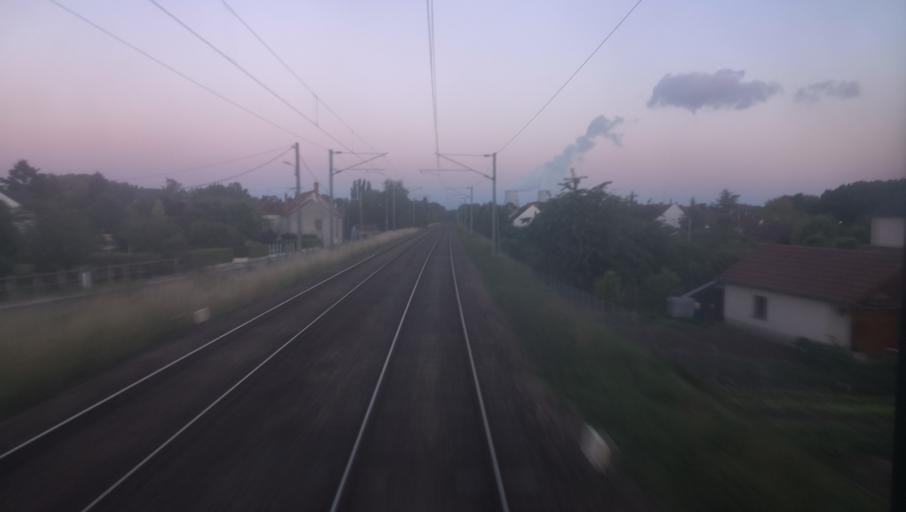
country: FR
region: Centre
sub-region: Departement du Loiret
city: Bonny-sur-Loire
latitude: 47.5537
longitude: 2.8489
